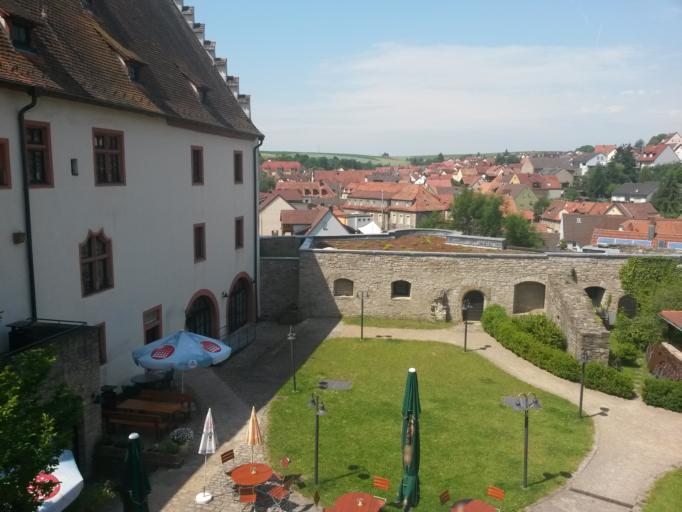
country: DE
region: Bavaria
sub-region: Regierungsbezirk Unterfranken
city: Rimpar
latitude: 49.8573
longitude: 9.9582
